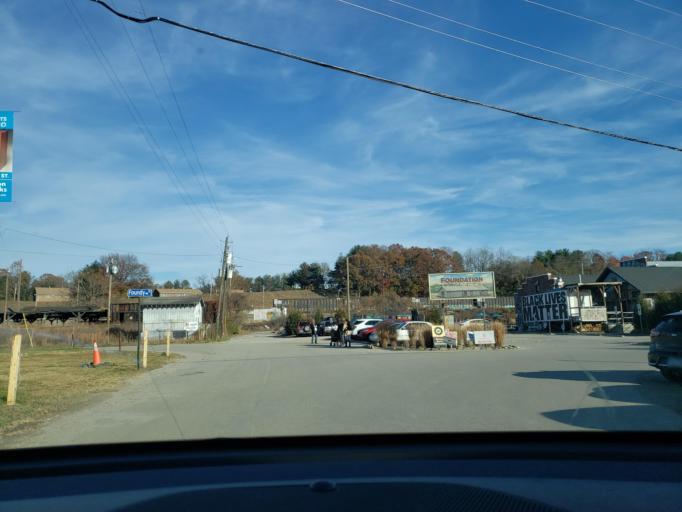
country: US
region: North Carolina
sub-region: Buncombe County
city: Asheville
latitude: 35.5780
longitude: -82.5668
